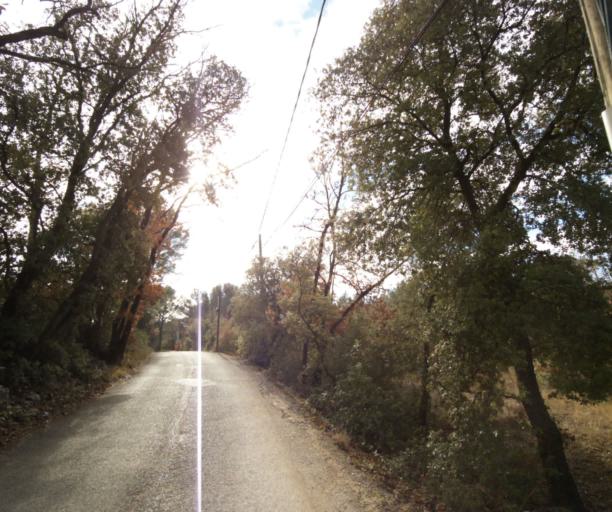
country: FR
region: Provence-Alpes-Cote d'Azur
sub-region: Departement du Var
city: Trans-en-Provence
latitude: 43.5162
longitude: 6.4950
